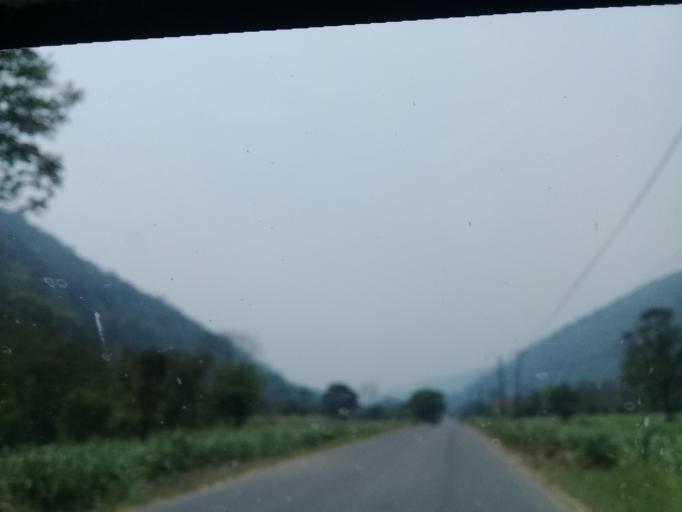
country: MX
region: Veracruz
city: Tezonapa
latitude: 18.6162
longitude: -96.6968
